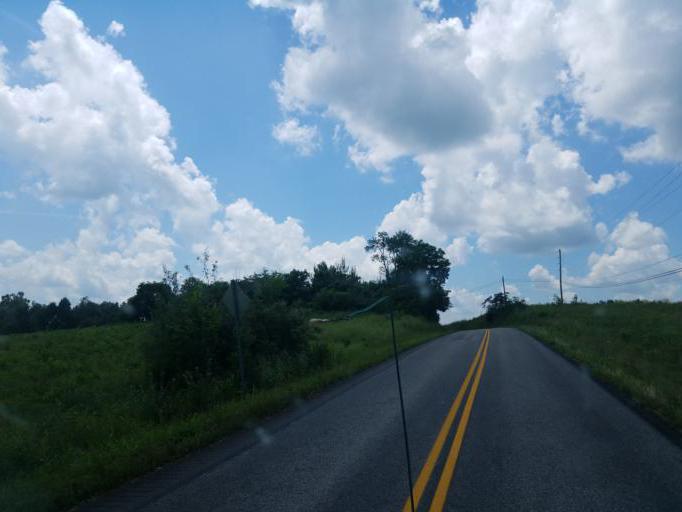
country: US
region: Kentucky
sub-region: Grayson County
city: Leitchfield
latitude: 37.4890
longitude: -86.4760
